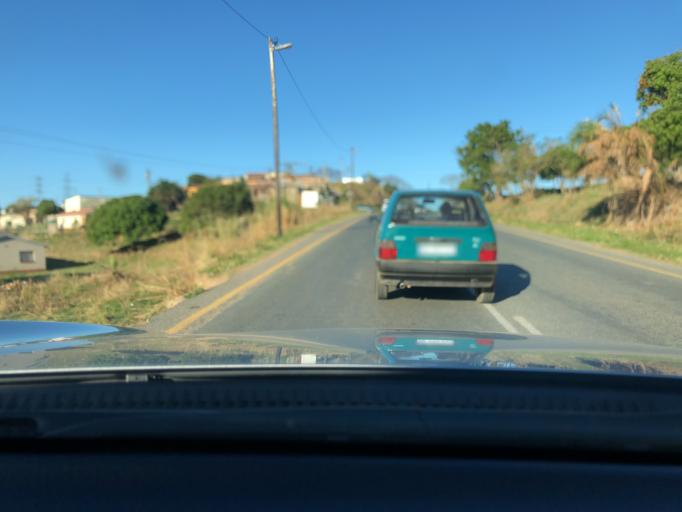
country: ZA
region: KwaZulu-Natal
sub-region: eThekwini Metropolitan Municipality
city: Umkomaas
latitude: -30.0361
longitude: 30.8691
